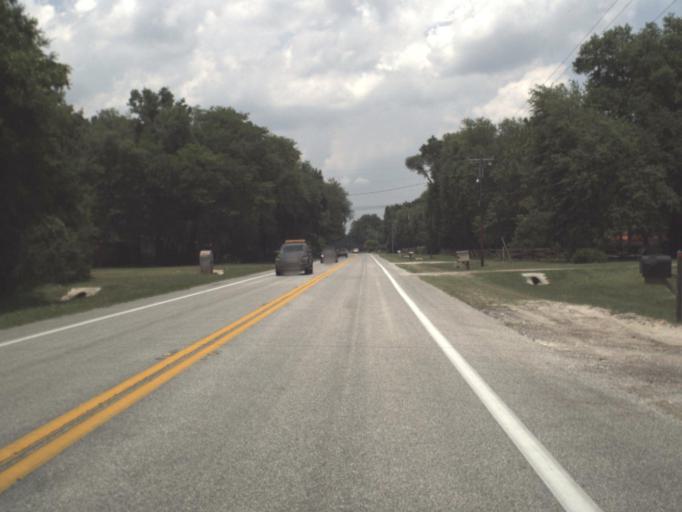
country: US
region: Florida
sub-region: Putnam County
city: Palatka
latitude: 29.6008
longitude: -81.7116
